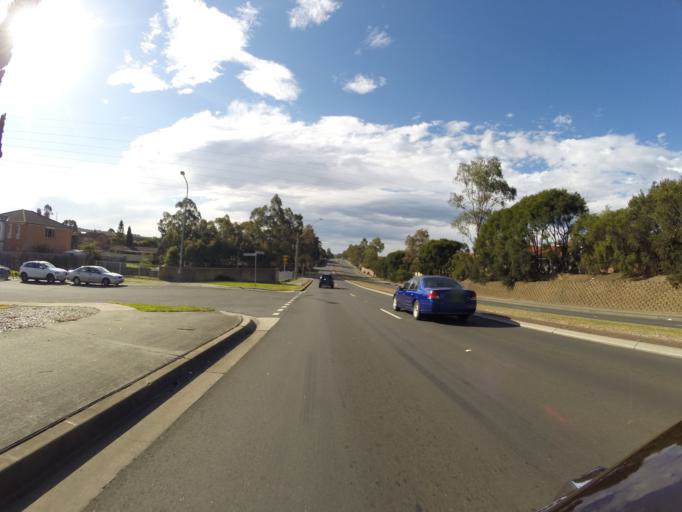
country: AU
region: New South Wales
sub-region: Fairfield
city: Cecil Park
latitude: -33.8806
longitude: 150.8662
